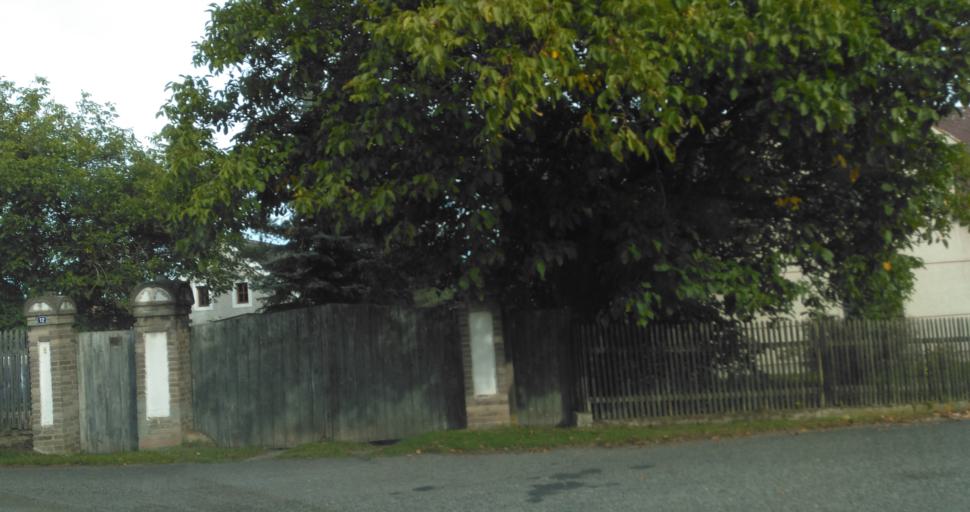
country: CZ
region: Central Bohemia
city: Pavlikov
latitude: 49.9652
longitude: 13.7668
